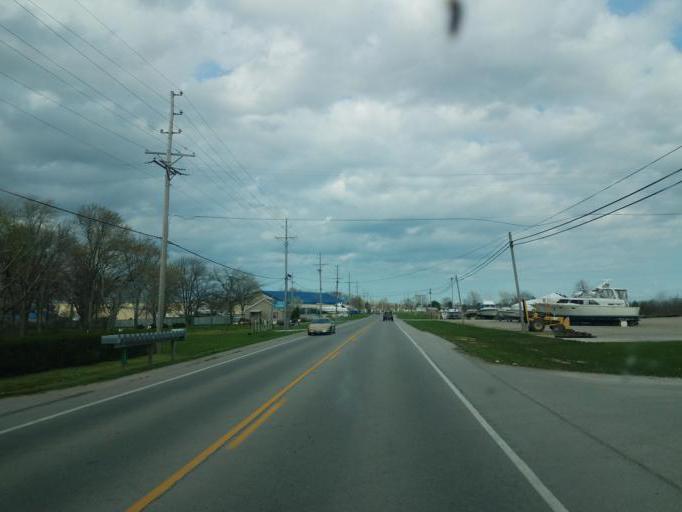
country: US
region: Ohio
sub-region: Erie County
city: Sandusky
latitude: 41.5315
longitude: -82.8075
